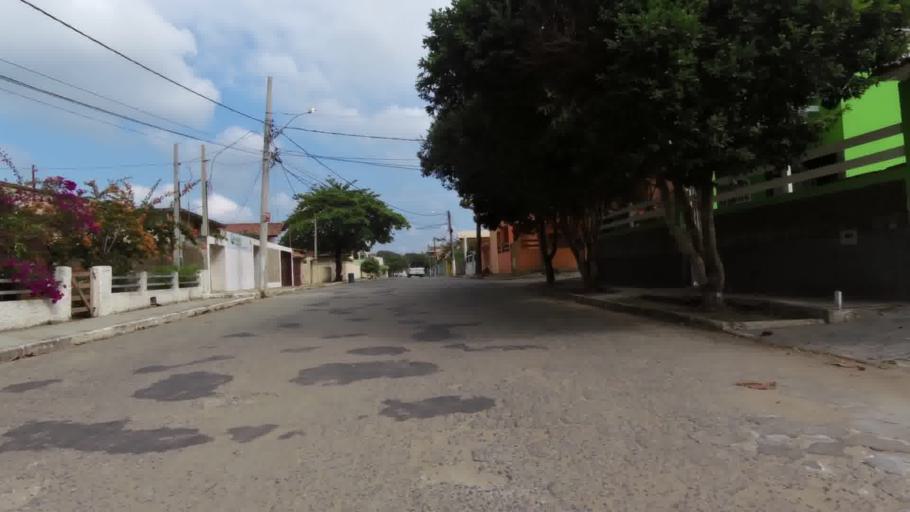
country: BR
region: Espirito Santo
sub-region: Marataizes
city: Marataizes
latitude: -21.0339
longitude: -40.8151
